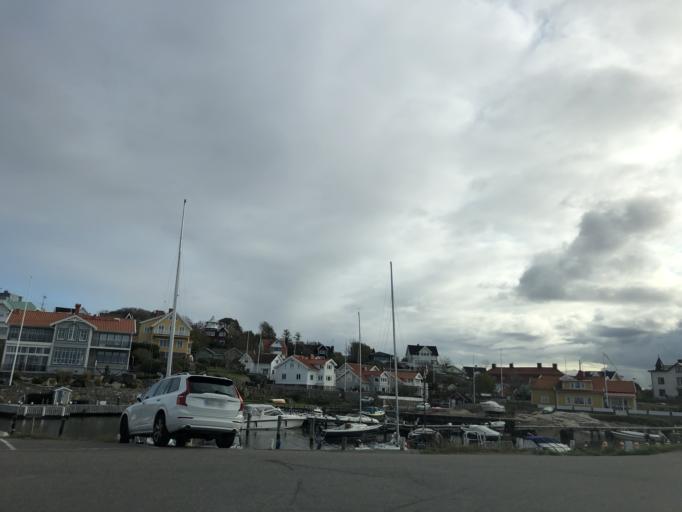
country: SE
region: Vaestra Goetaland
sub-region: Goteborg
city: Majorna
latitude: 57.6701
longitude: 11.8499
